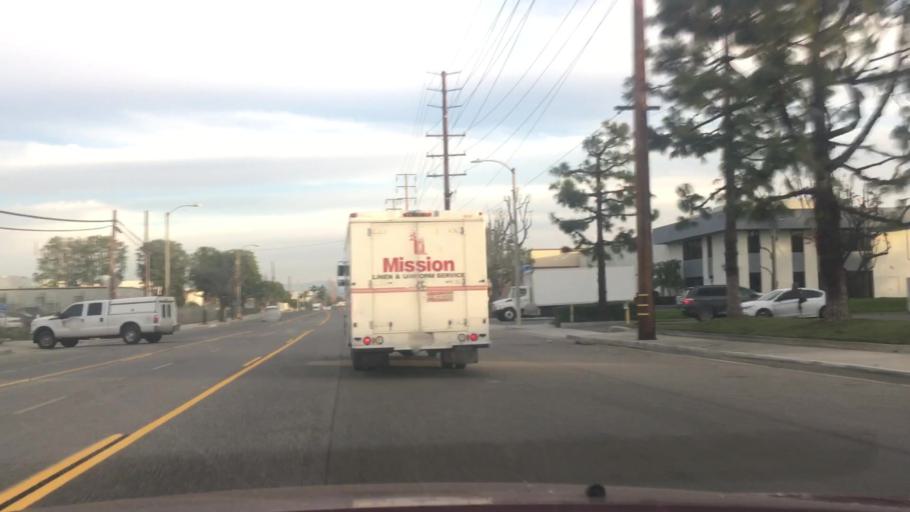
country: US
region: California
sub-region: Orange County
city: Buena Park
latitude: 33.8761
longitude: -118.0114
